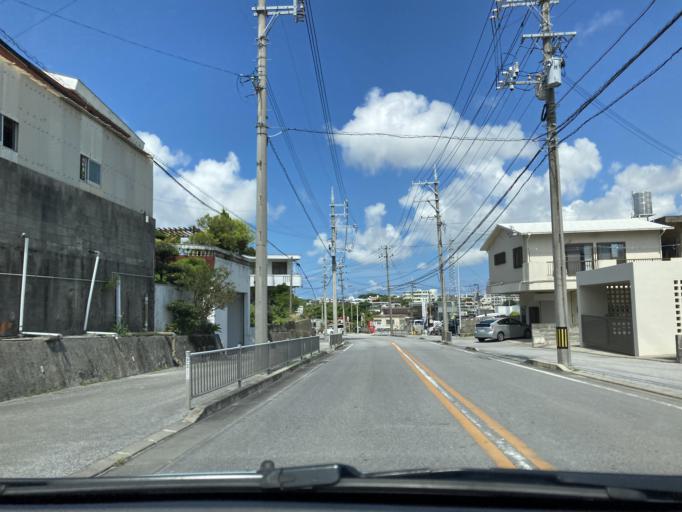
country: JP
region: Okinawa
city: Tomigusuku
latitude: 26.1648
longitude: 127.7227
